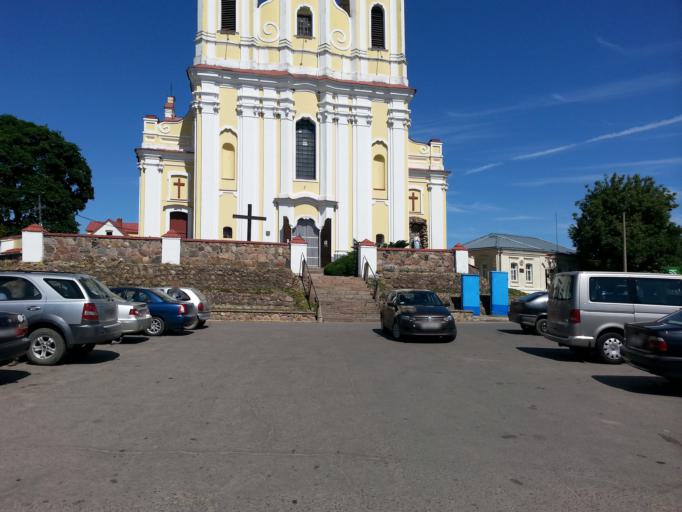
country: BY
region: Vitebsk
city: Hlybokaye
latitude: 55.1406
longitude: 27.6940
